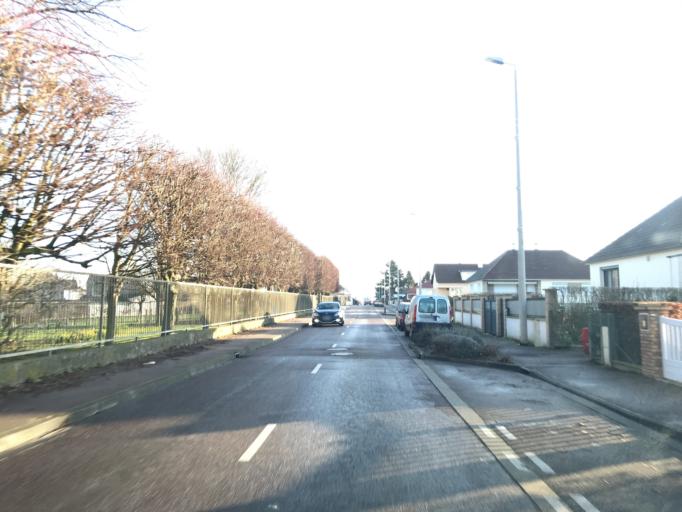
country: FR
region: Haute-Normandie
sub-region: Departement de la Seine-Maritime
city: Le Petit-Quevilly
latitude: 49.4061
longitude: 1.0580
